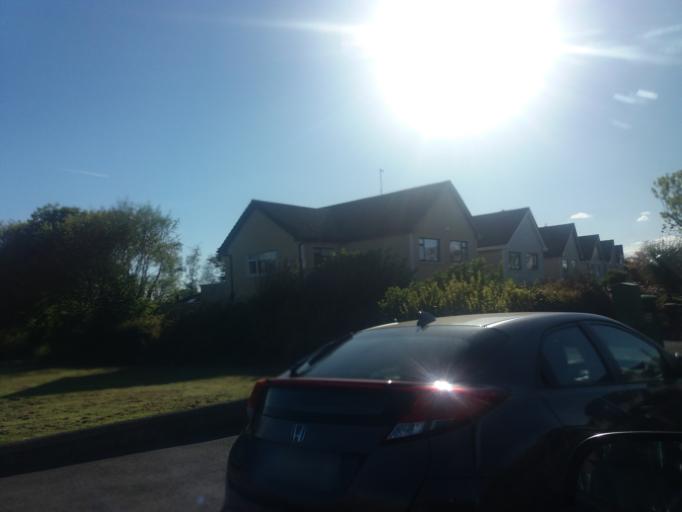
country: IE
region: Leinster
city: Sutton
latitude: 53.3774
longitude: -6.0996
